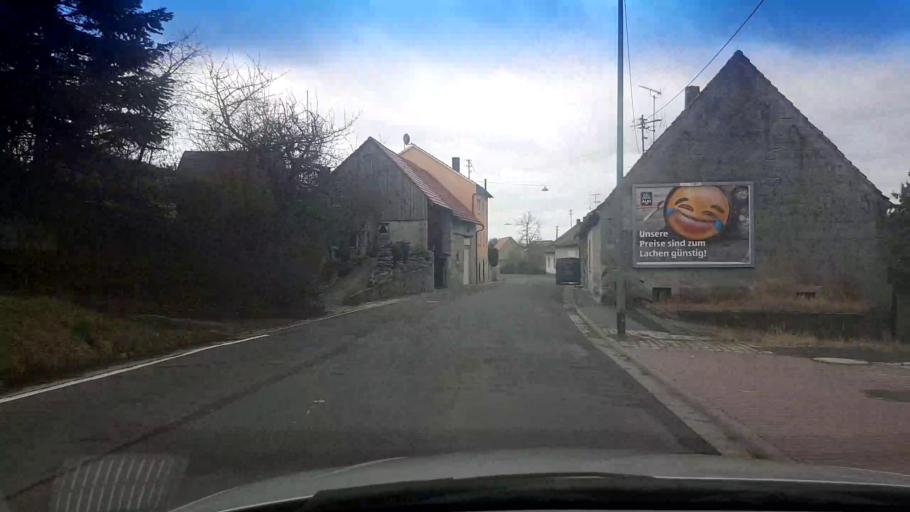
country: DE
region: Bavaria
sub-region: Regierungsbezirk Unterfranken
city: Eltmann
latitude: 49.9325
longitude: 10.6492
